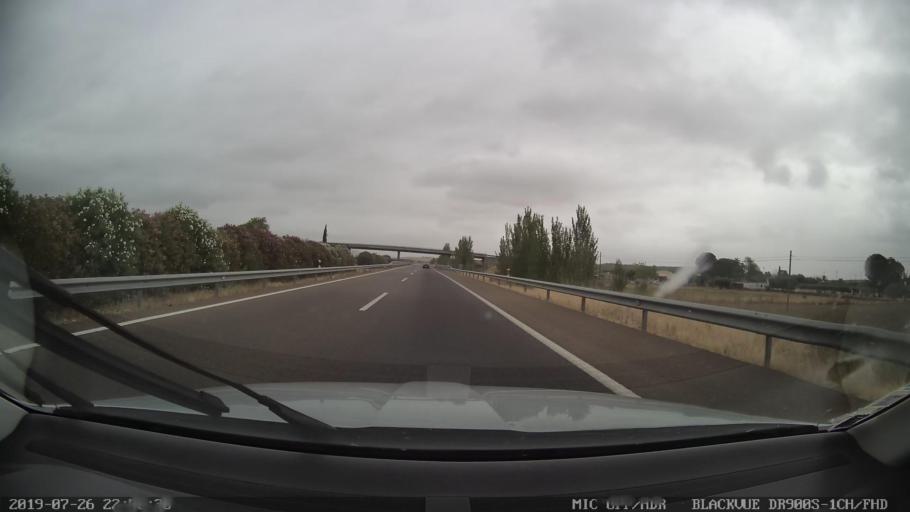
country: ES
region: Extremadura
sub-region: Provincia de Badajoz
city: Calamonte
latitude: 38.8970
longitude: -6.4150
